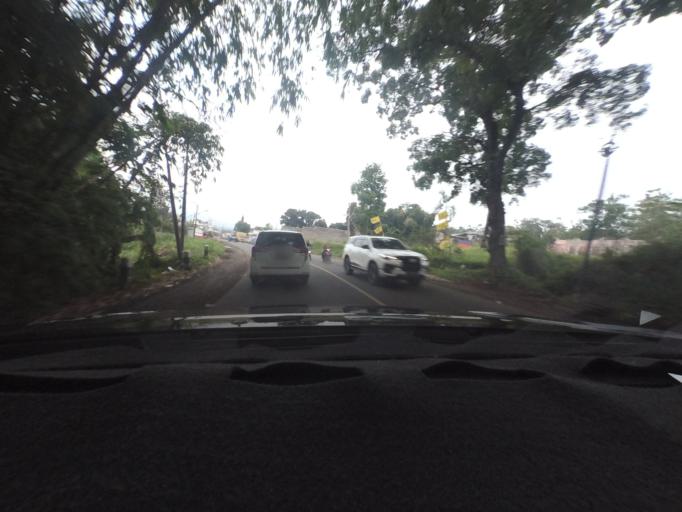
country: ID
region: West Java
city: Cicurug
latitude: -6.8206
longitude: 106.7651
